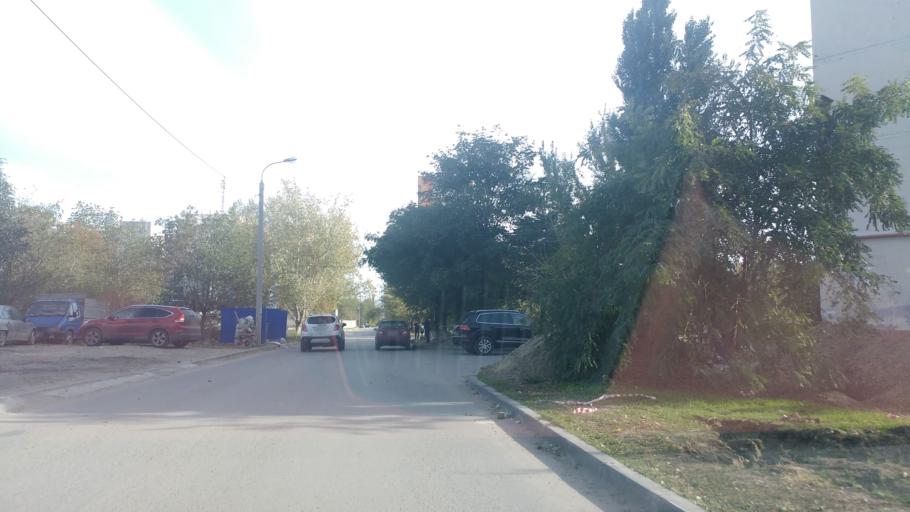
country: RU
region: Volgograd
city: Volgograd
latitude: 48.7655
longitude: 44.5474
